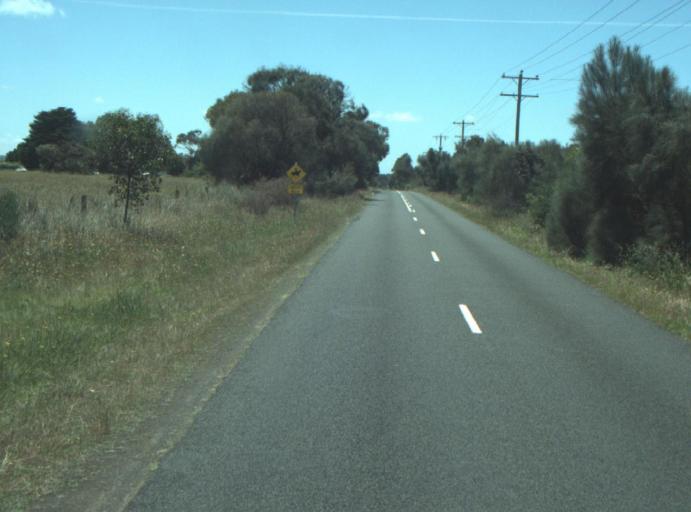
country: AU
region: Victoria
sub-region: Greater Geelong
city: Clifton Springs
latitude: -38.2367
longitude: 144.5771
